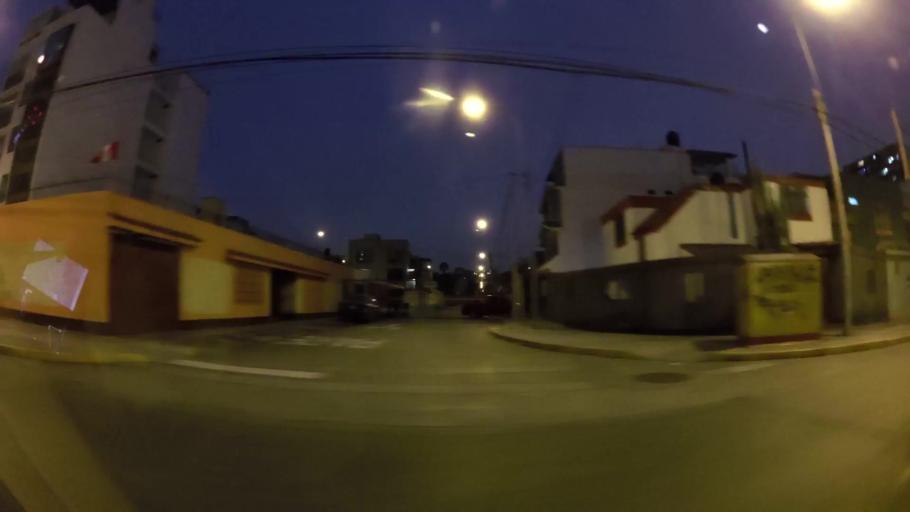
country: PE
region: Callao
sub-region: Callao
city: Callao
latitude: -12.0731
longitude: -77.0920
